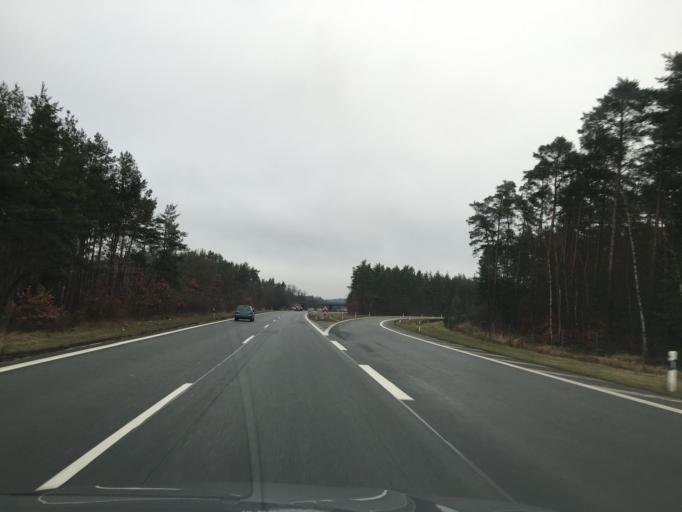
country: DE
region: Bavaria
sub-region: Regierungsbezirk Mittelfranken
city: Rothenbach an der Pegnitz
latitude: 49.4545
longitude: 11.2405
